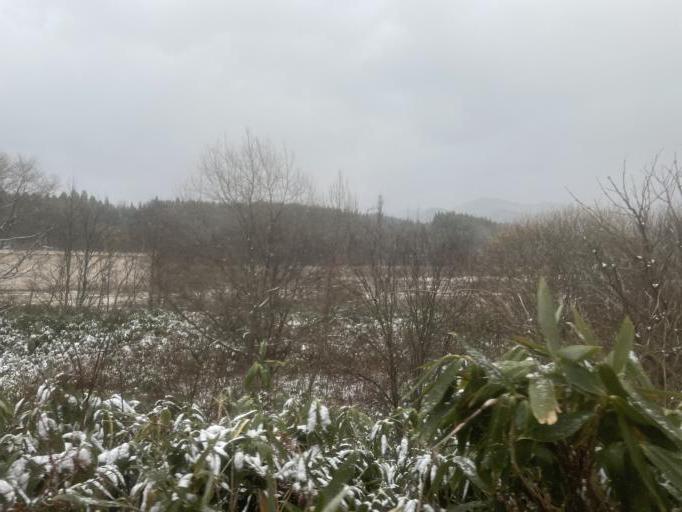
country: JP
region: Aomori
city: Goshogawara
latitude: 41.1391
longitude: 140.5178
